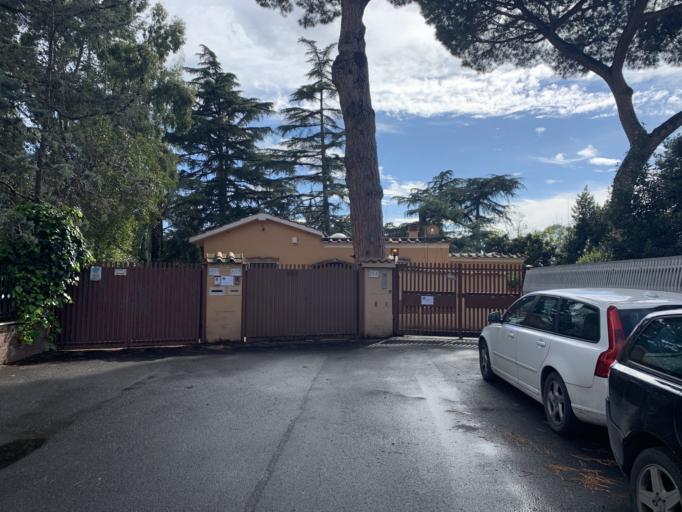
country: VA
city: Vatican City
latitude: 41.8782
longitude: 12.4176
